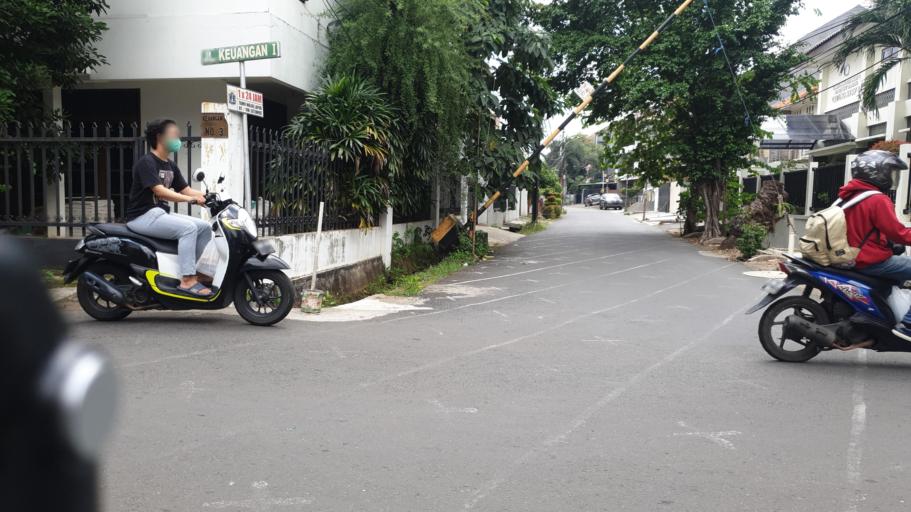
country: ID
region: Banten
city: South Tangerang
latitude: -6.2874
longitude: 106.7941
